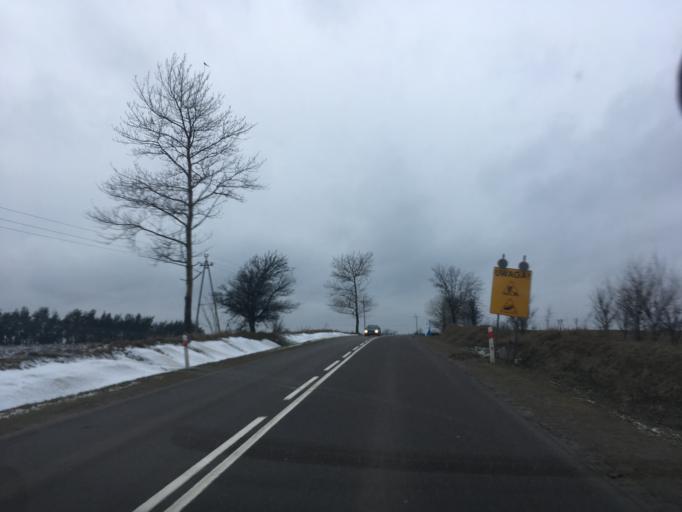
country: PL
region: Podlasie
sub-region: Suwalki
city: Suwalki
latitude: 54.1056
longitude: 22.8861
